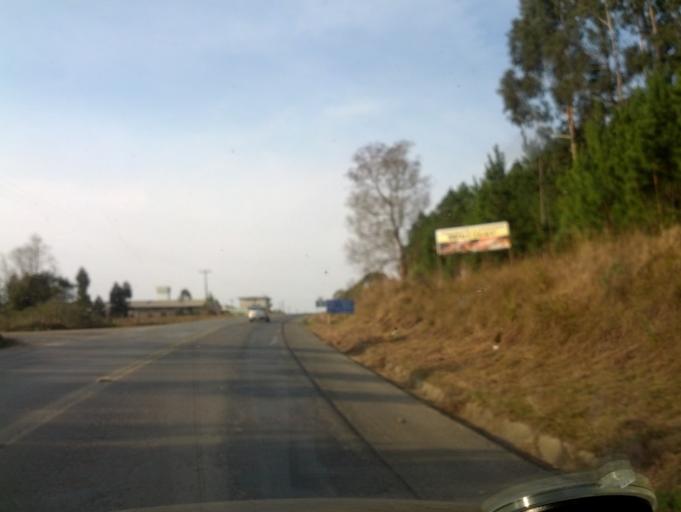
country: BR
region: Santa Catarina
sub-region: Otacilio Costa
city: Otacilio Costa
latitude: -27.5840
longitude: -50.1648
